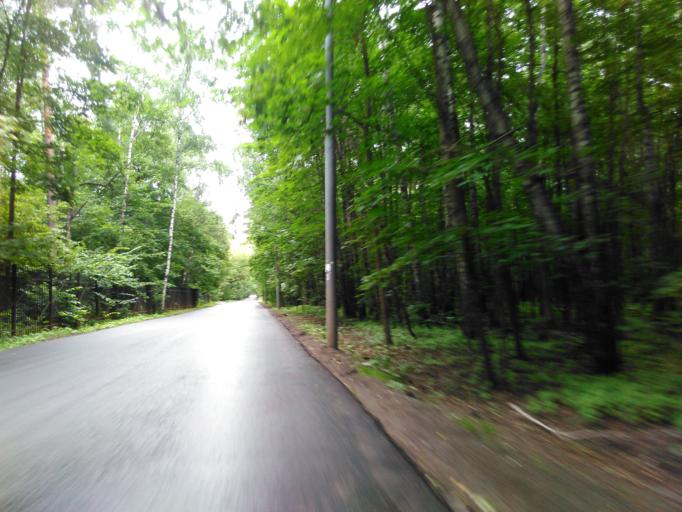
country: RU
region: Moscow
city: Rostokino
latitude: 55.8305
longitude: 37.6814
